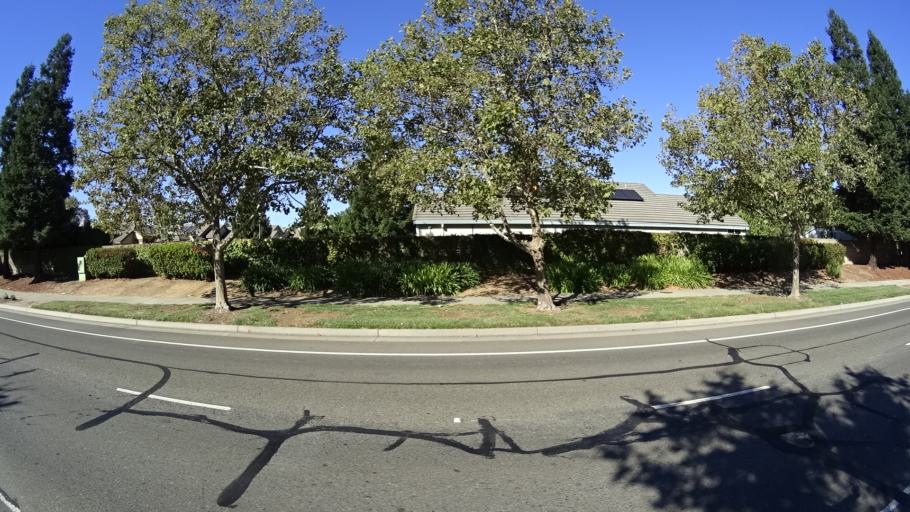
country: US
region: California
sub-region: Sacramento County
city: Vineyard
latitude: 38.4467
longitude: -121.3717
